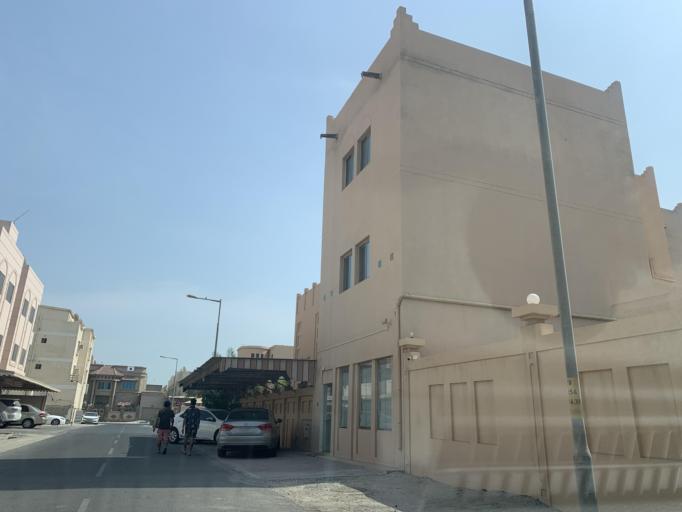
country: BH
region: Muharraq
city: Al Hadd
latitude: 26.2657
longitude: 50.6561
